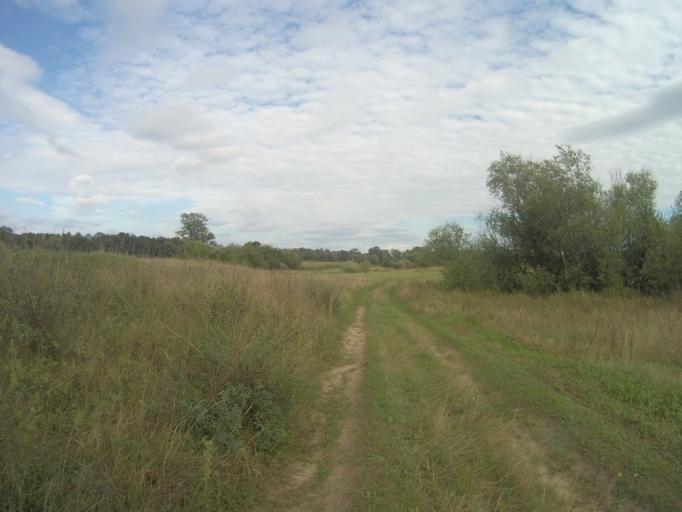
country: RU
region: Vladimir
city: Raduzhnyy
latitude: 56.0395
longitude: 40.2836
